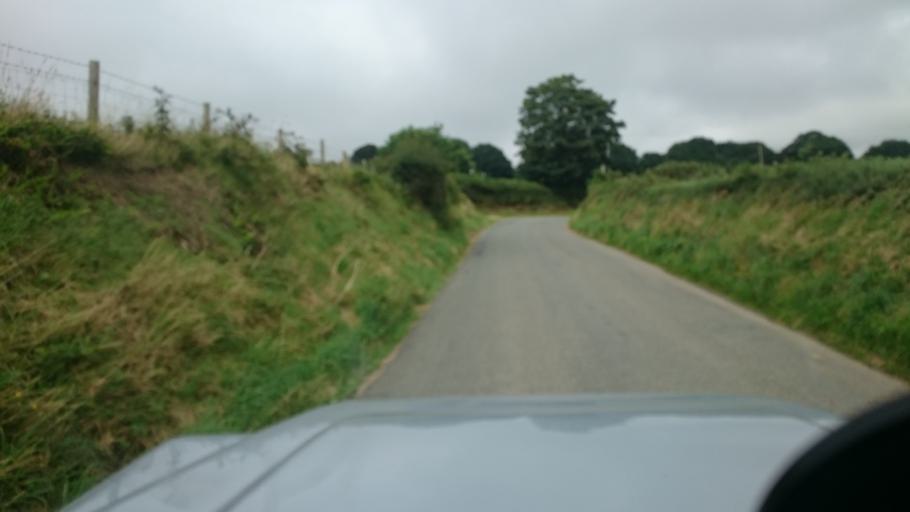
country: GB
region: Wales
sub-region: Pembrokeshire
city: Ambleston
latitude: 51.9228
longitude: -4.9440
